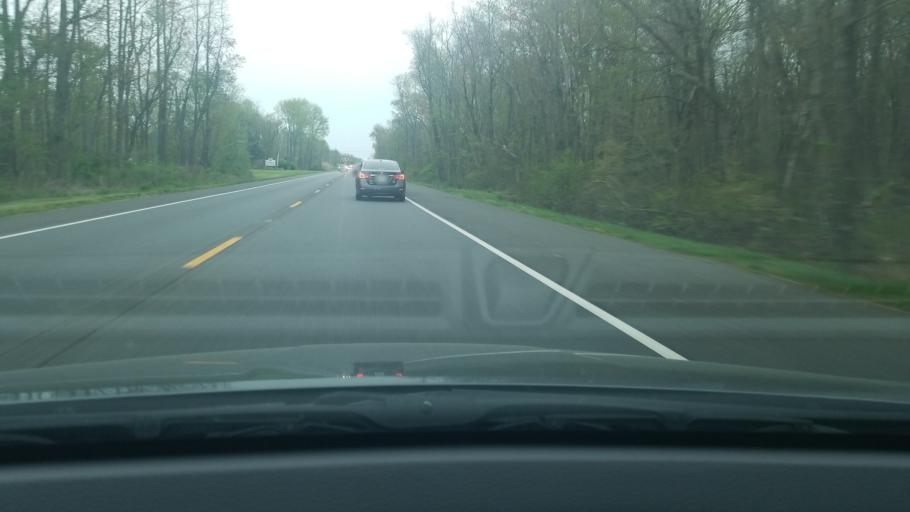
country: US
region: New Jersey
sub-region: Burlington County
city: Mount Laurel
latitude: 39.8975
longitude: -74.8619
